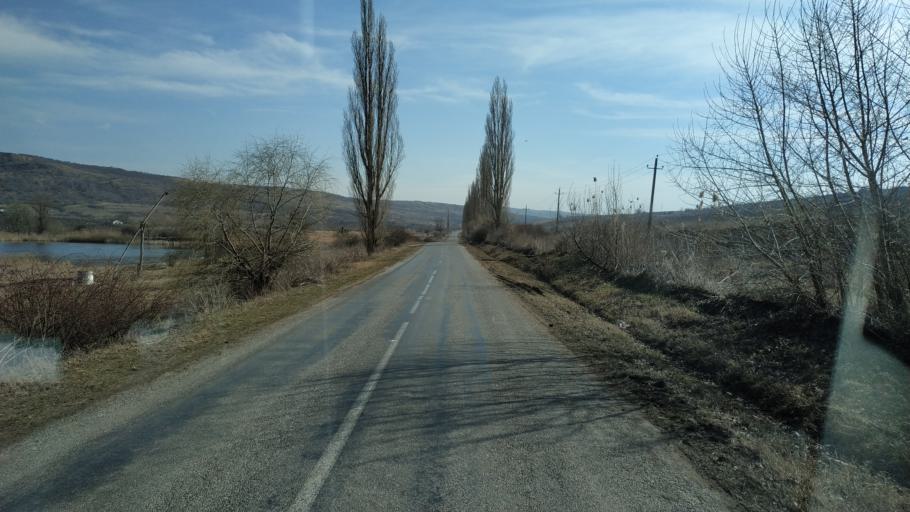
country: MD
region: Nisporeni
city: Nisporeni
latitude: 47.1717
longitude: 28.0905
